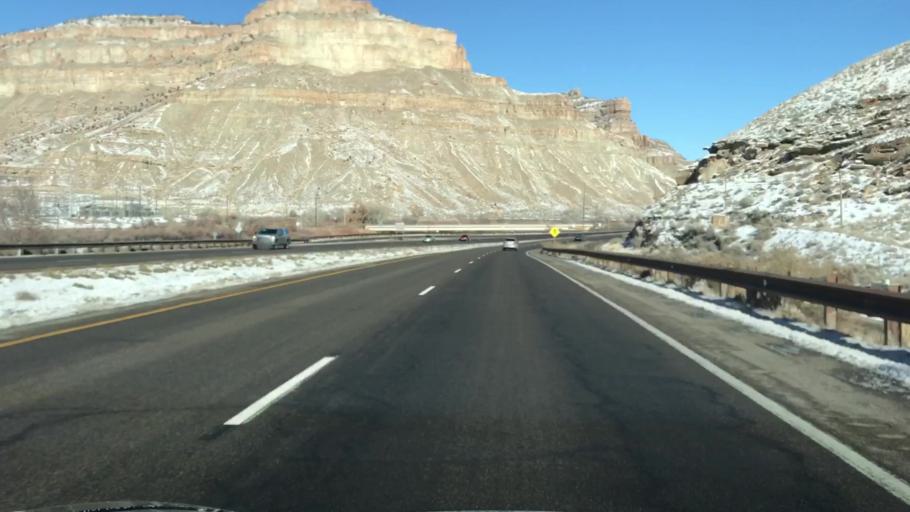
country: US
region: Colorado
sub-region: Mesa County
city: Palisade
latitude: 39.1440
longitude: -108.3156
